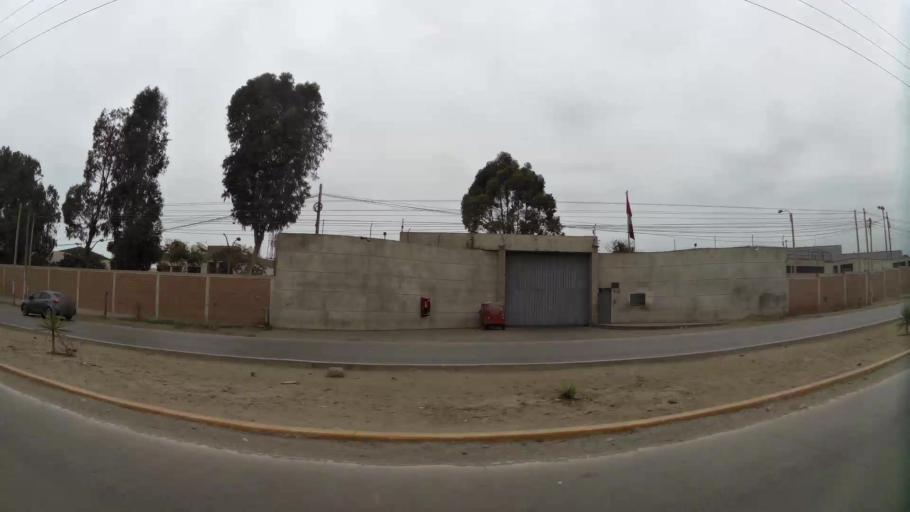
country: PE
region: Lima
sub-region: Lima
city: Surco
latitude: -12.2109
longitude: -76.9615
